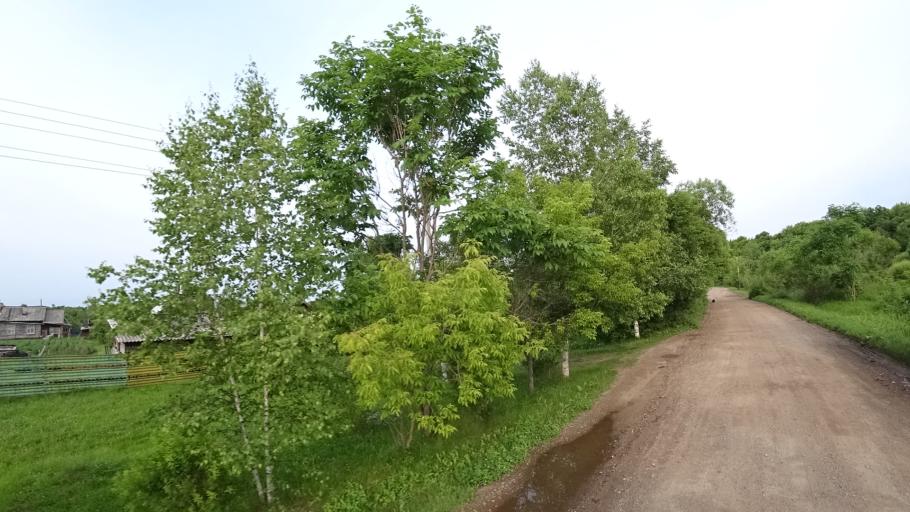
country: RU
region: Primorskiy
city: Novosysoyevka
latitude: 44.2435
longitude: 133.3615
